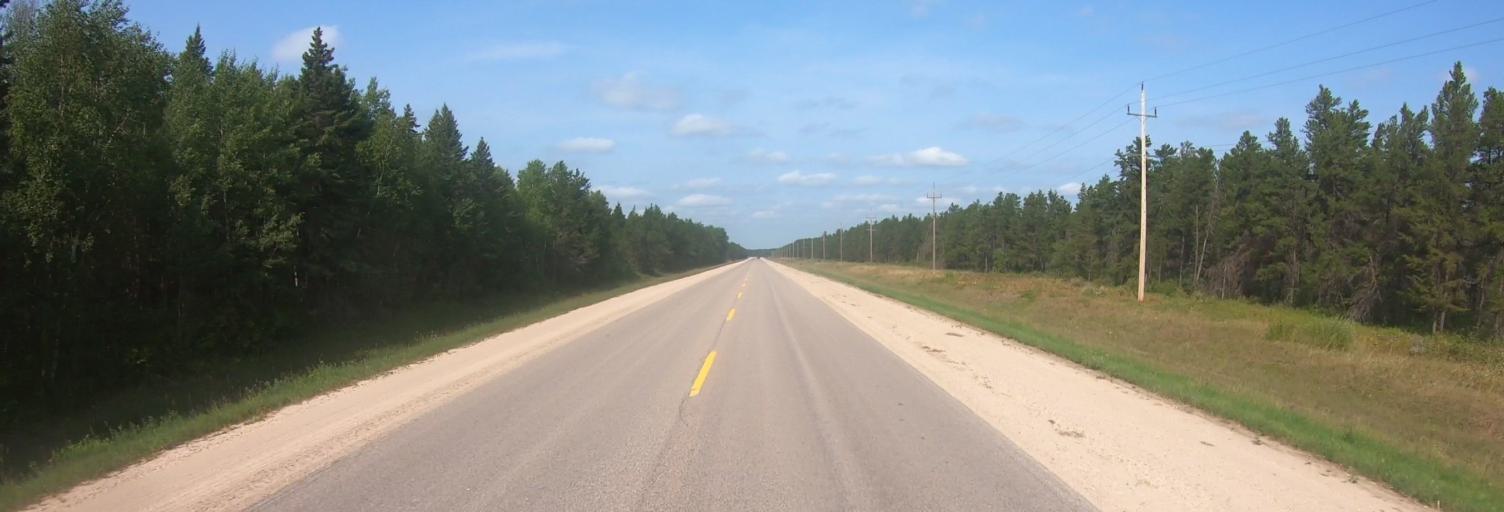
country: CA
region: Manitoba
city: La Broquerie
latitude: 49.1777
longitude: -96.1826
